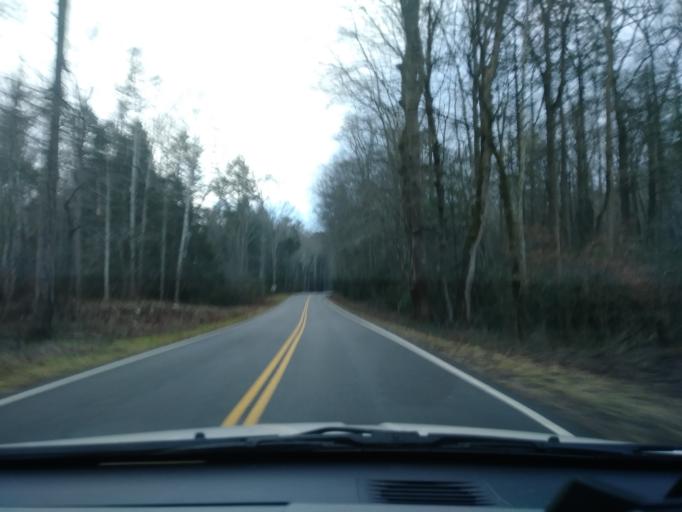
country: US
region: Tennessee
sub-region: Unicoi County
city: Unicoi
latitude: 36.1748
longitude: -82.3004
